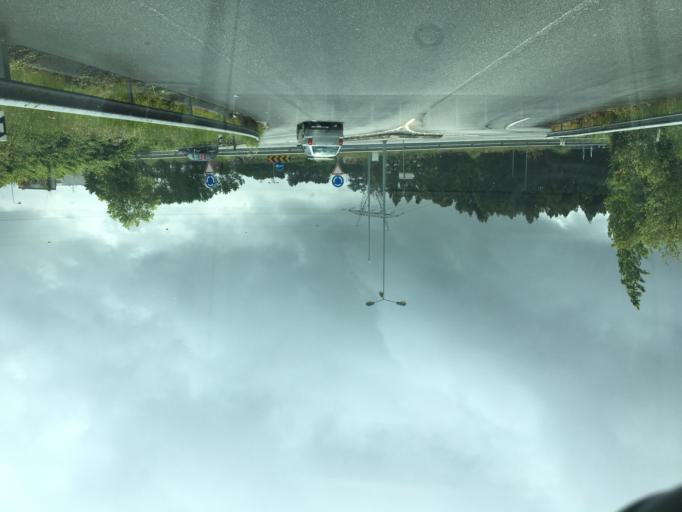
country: PT
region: Porto
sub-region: Maia
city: Nogueira
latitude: 41.2406
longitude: -8.5995
